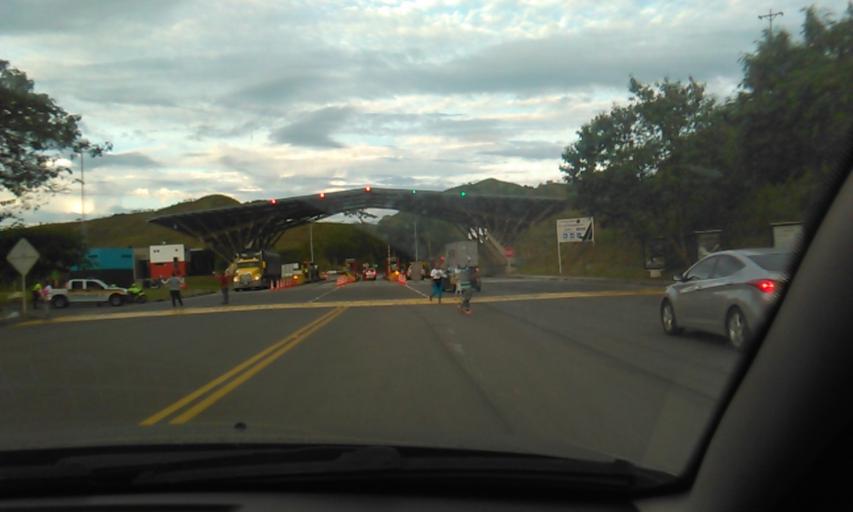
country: CO
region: Valle del Cauca
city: Caicedonia
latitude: 4.4078
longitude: -75.9002
